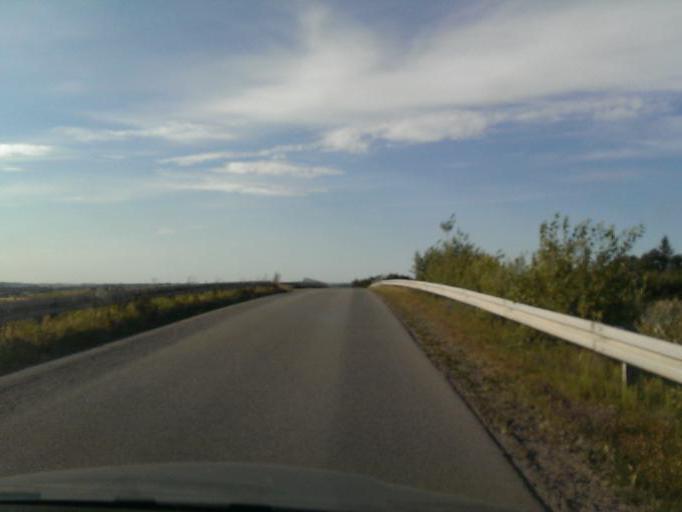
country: DK
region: Central Jutland
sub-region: Arhus Kommune
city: Kolt
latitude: 56.1208
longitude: 10.0505
